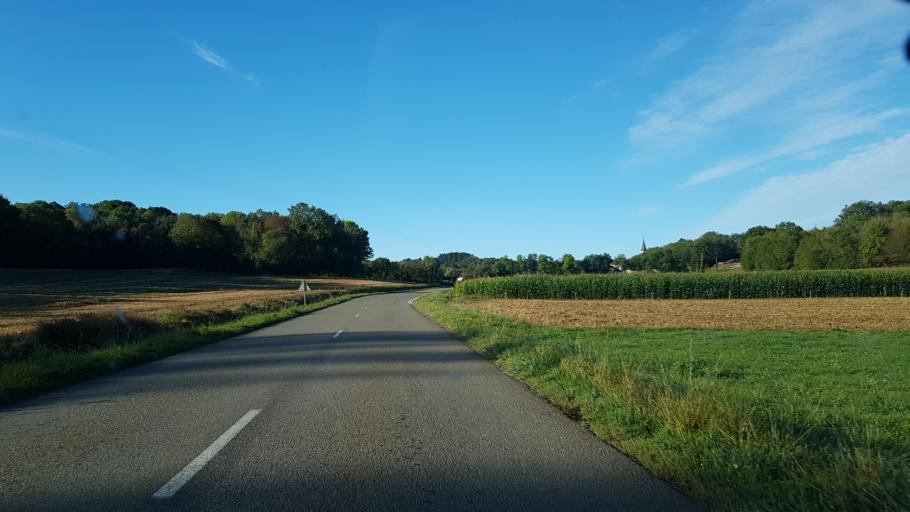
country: FR
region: Franche-Comte
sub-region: Departement du Jura
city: Cousance
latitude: 46.5583
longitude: 5.4996
